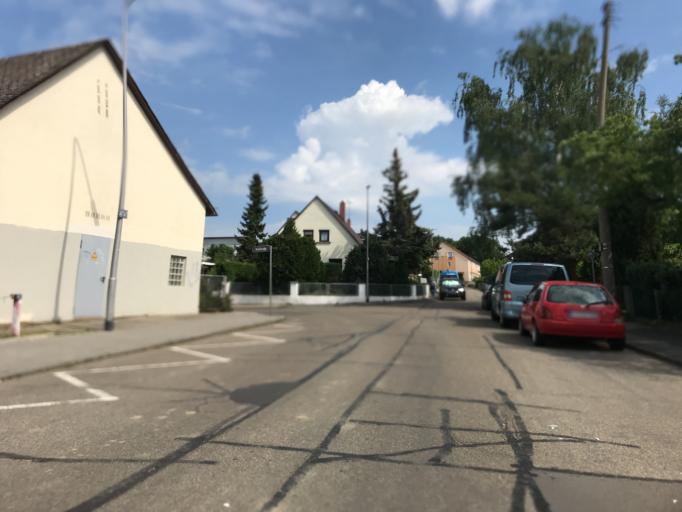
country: DE
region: Hesse
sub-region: Regierungsbezirk Darmstadt
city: Walluf
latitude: 50.0874
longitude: 8.1907
